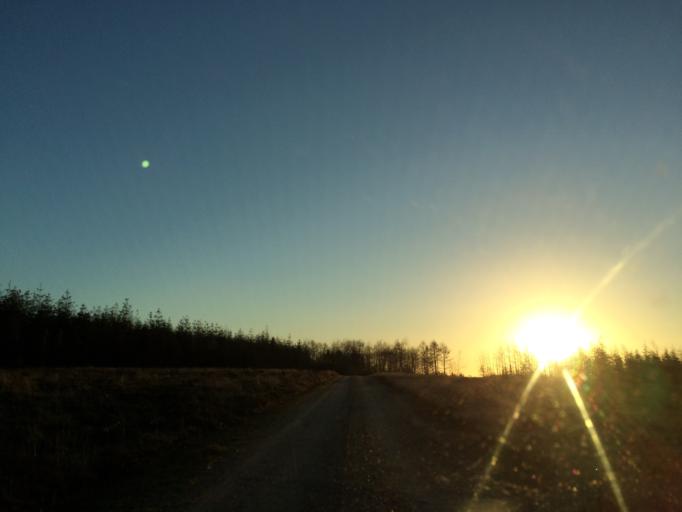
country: DK
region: Central Jutland
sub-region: Ringkobing-Skjern Kommune
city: Videbaek
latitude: 56.2182
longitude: 8.5192
